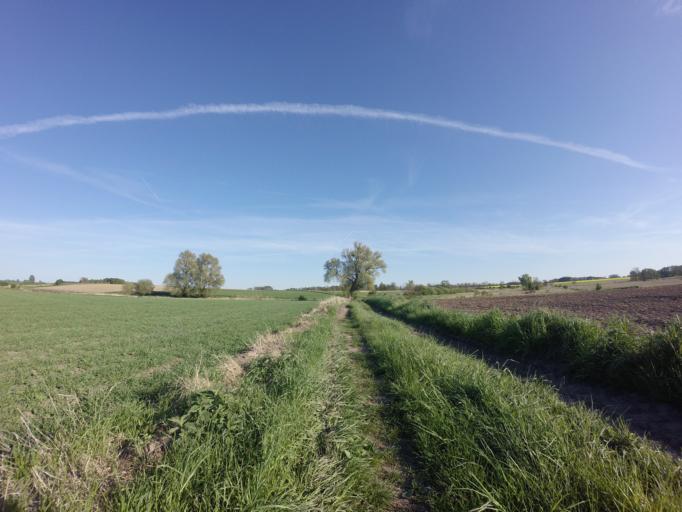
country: PL
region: West Pomeranian Voivodeship
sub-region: Powiat choszczenski
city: Choszczno
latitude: 53.1166
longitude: 15.3545
